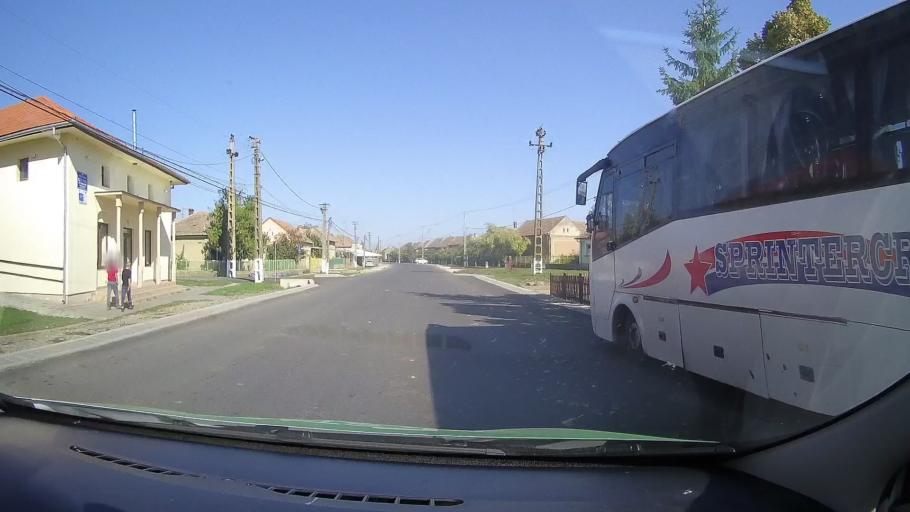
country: RO
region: Satu Mare
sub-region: Comuna Berveni
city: Berveni
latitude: 47.7558
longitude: 22.4725
